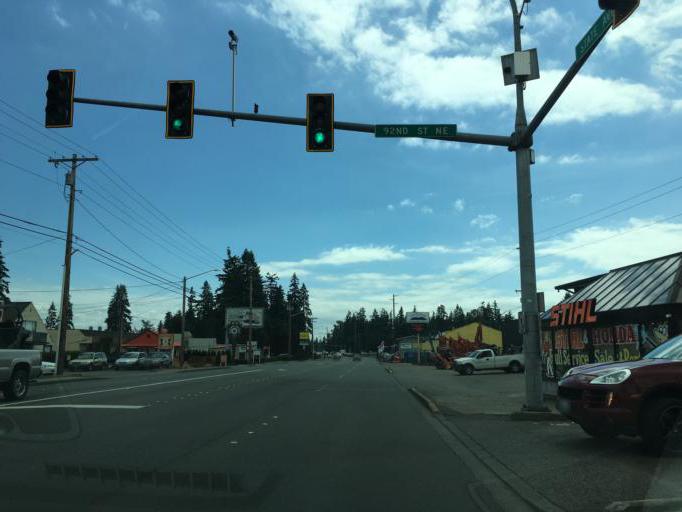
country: US
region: Washington
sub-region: Snohomish County
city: Marysville
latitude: 48.0793
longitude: -122.1751
